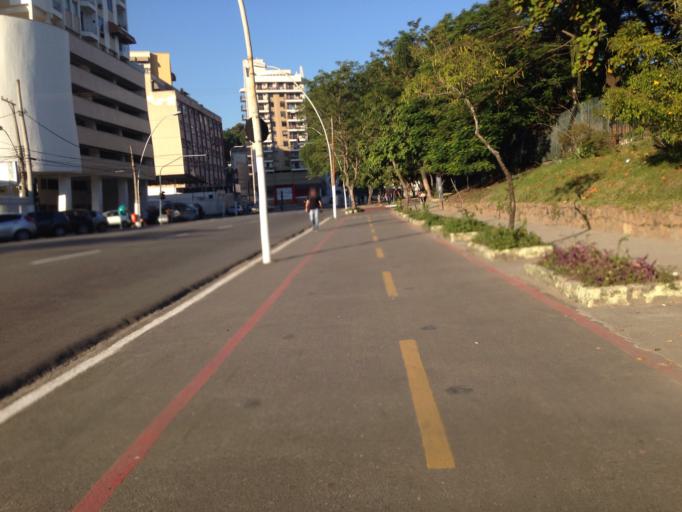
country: BR
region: Rio de Janeiro
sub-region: Niteroi
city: Niteroi
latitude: -22.8939
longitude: -43.1149
